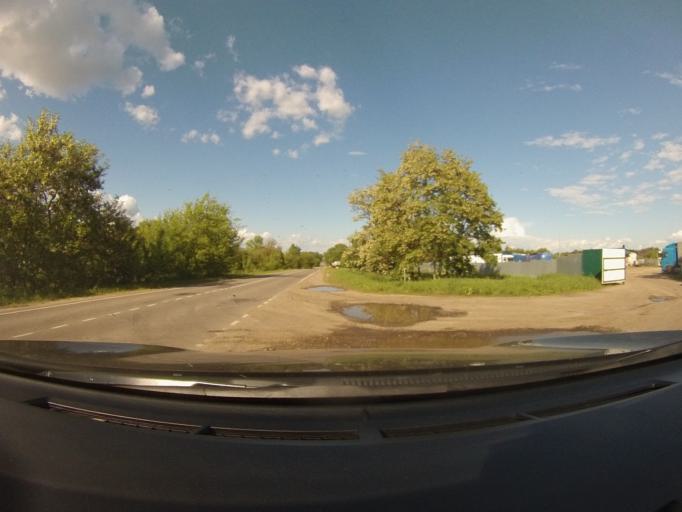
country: RU
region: Orjol
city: Mtsensk
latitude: 53.3009
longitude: 36.6190
